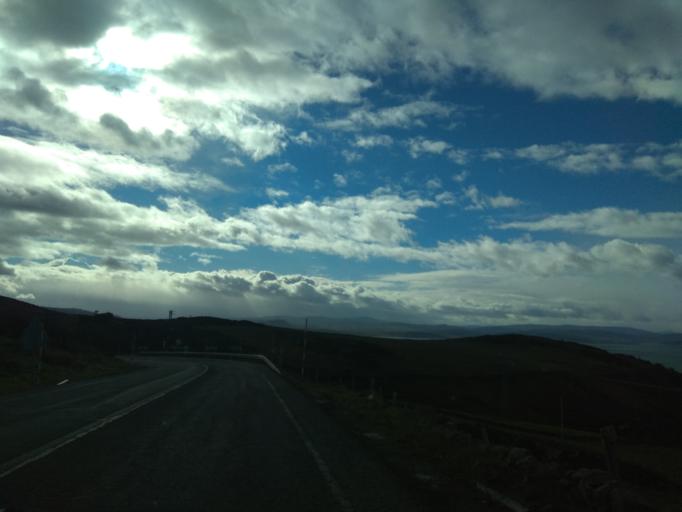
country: ES
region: Castille and Leon
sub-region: Provincia de Burgos
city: Arija
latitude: 43.0435
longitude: -3.8786
